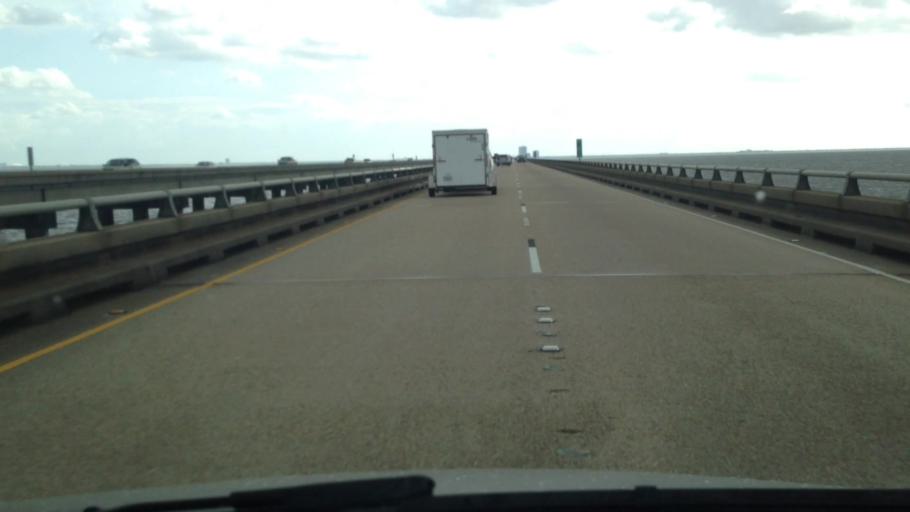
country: US
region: Louisiana
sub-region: Jefferson Parish
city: Metairie
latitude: 30.1027
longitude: -90.1399
